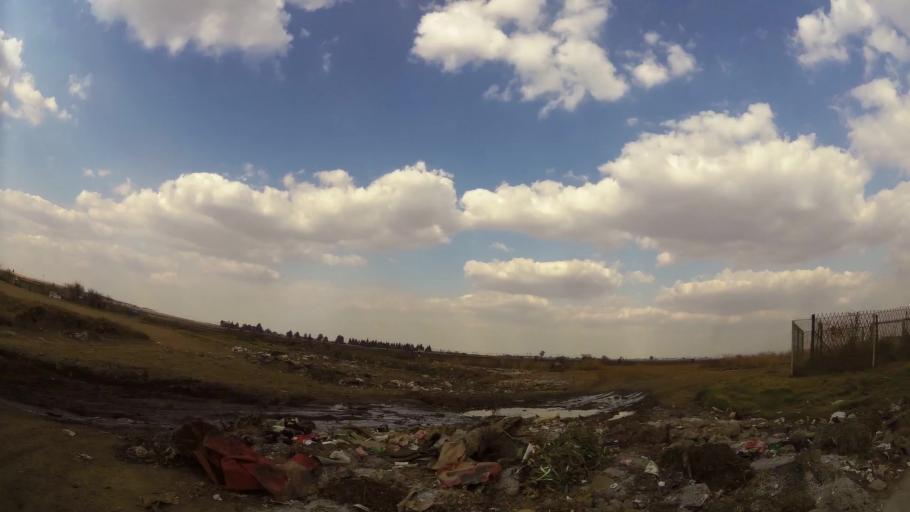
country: ZA
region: Mpumalanga
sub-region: Nkangala District Municipality
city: Delmas
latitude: -26.1433
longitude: 28.6944
